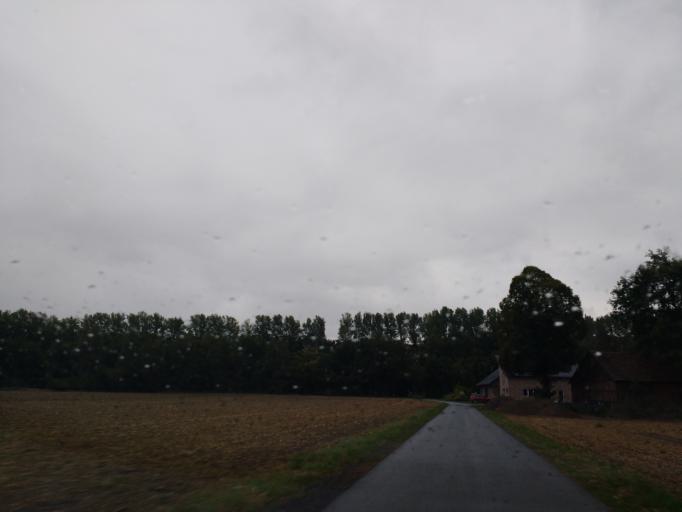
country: DE
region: North Rhine-Westphalia
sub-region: Regierungsbezirk Arnsberg
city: Lippstadt
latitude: 51.7213
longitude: 8.3990
